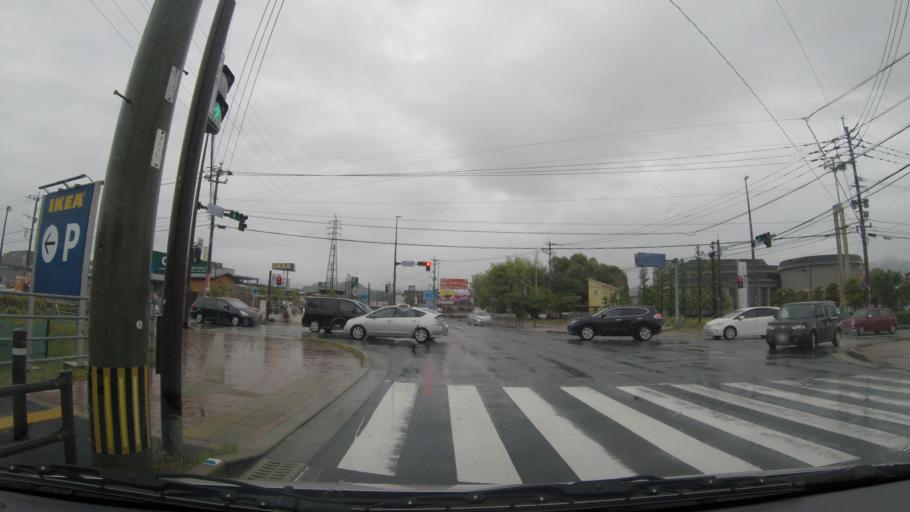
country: JP
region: Fukuoka
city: Shingu
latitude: 33.7082
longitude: 130.4517
